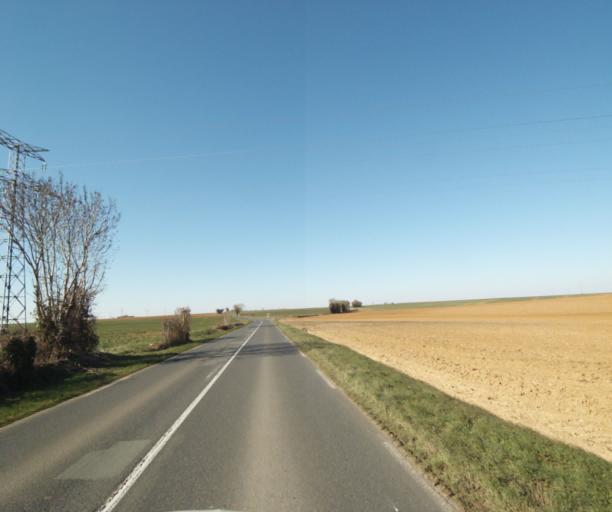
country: FR
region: Poitou-Charentes
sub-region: Departement des Deux-Sevres
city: Saint-Maxire
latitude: 46.3613
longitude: -0.4867
